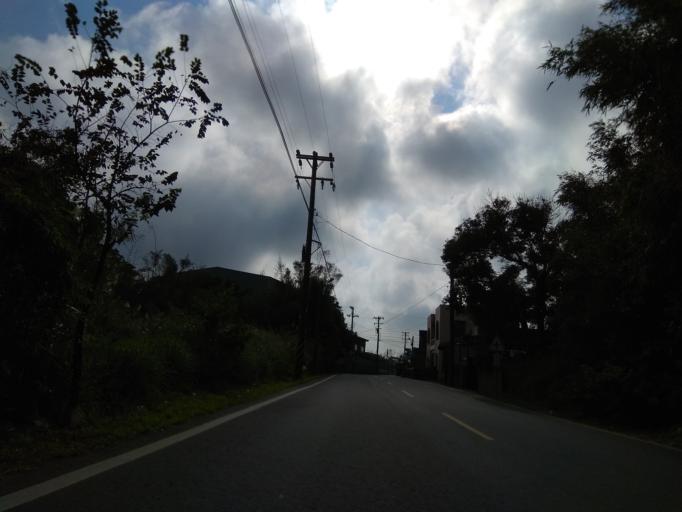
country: TW
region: Taiwan
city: Taoyuan City
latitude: 25.0568
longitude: 121.1506
